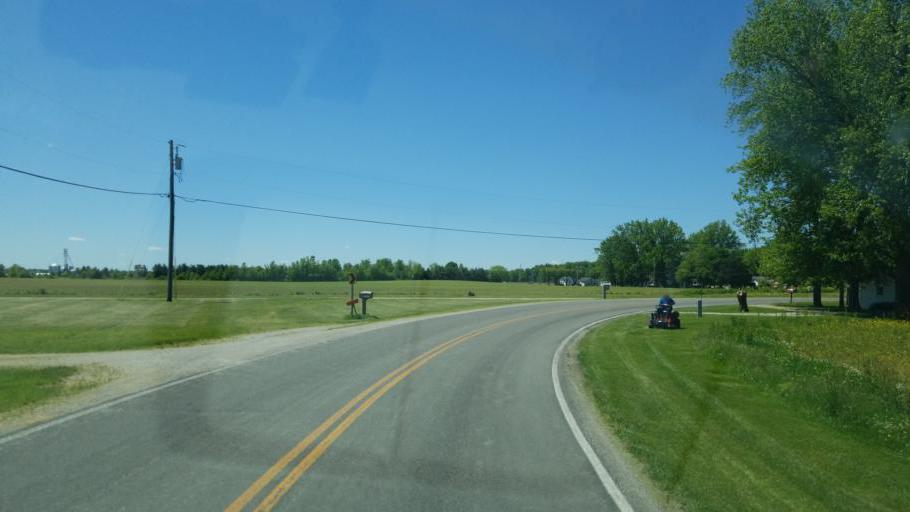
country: US
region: Ohio
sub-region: Shelby County
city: Fort Loramie
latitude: 40.3672
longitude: -84.3365
